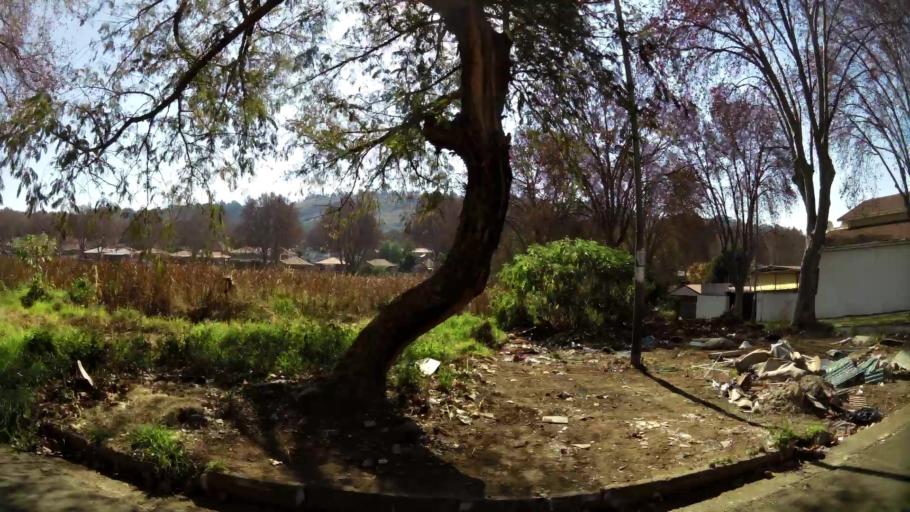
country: ZA
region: Gauteng
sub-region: City of Johannesburg Metropolitan Municipality
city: Johannesburg
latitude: -26.1906
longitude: 28.0780
